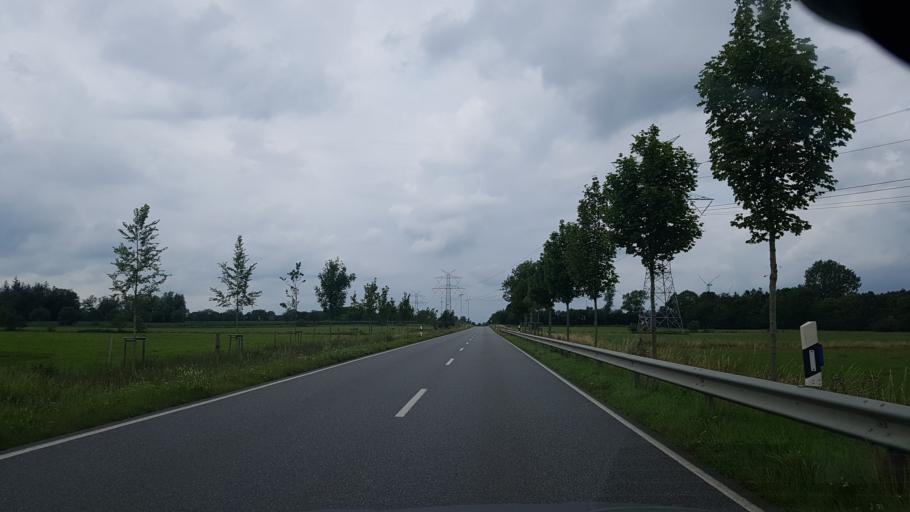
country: DE
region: Schleswig-Holstein
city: Jardelund
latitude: 54.8278
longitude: 9.2182
